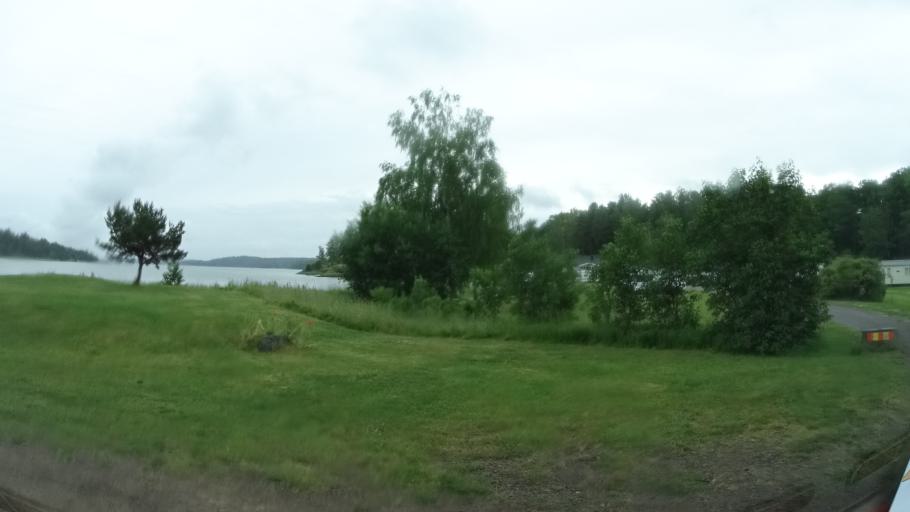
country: SE
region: Kalmar
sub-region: Vasterviks Kommun
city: Gamleby
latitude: 57.8889
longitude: 16.4177
